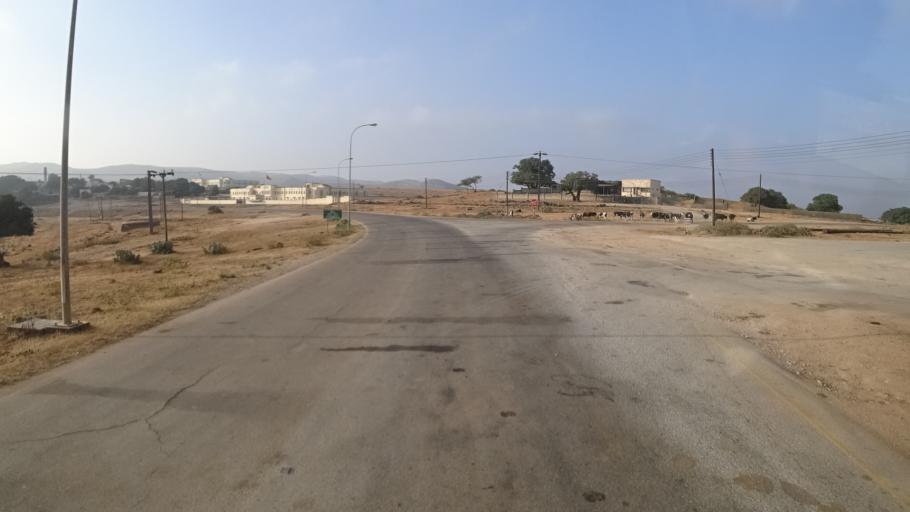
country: OM
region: Zufar
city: Salalah
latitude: 17.1243
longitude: 53.9989
